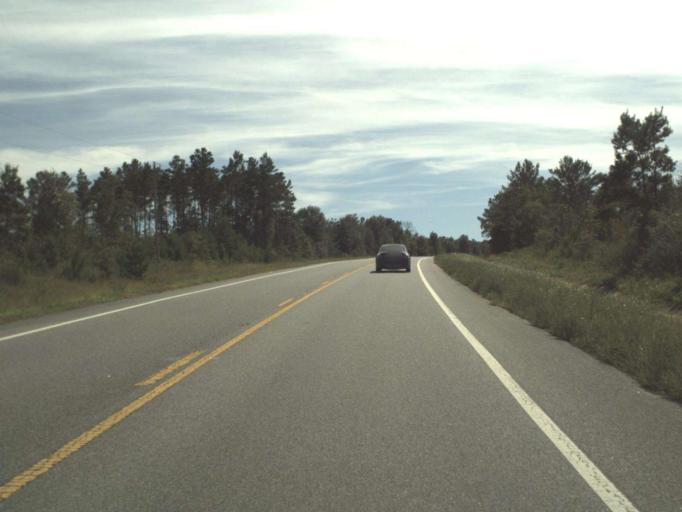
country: US
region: Florida
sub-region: Washington County
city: Chipley
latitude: 30.5953
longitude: -85.5935
